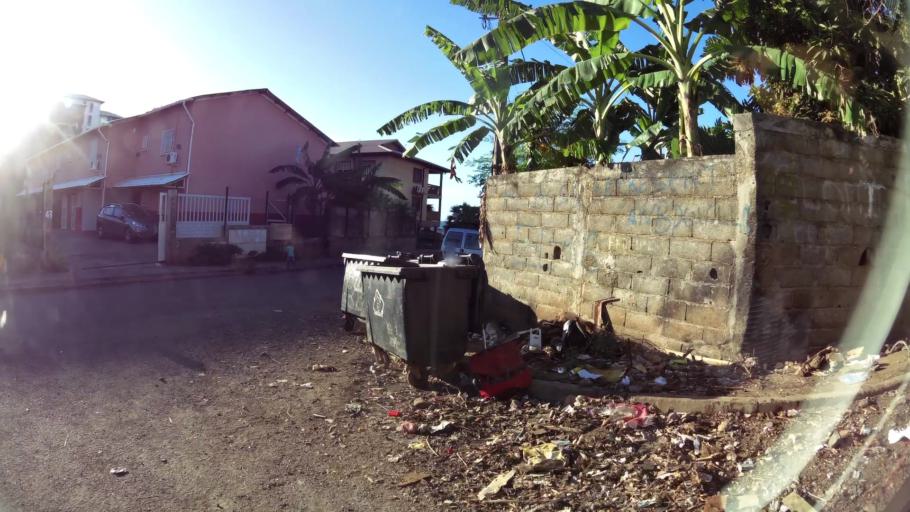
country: YT
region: Koungou
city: Koungou
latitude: -12.7332
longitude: 45.2059
